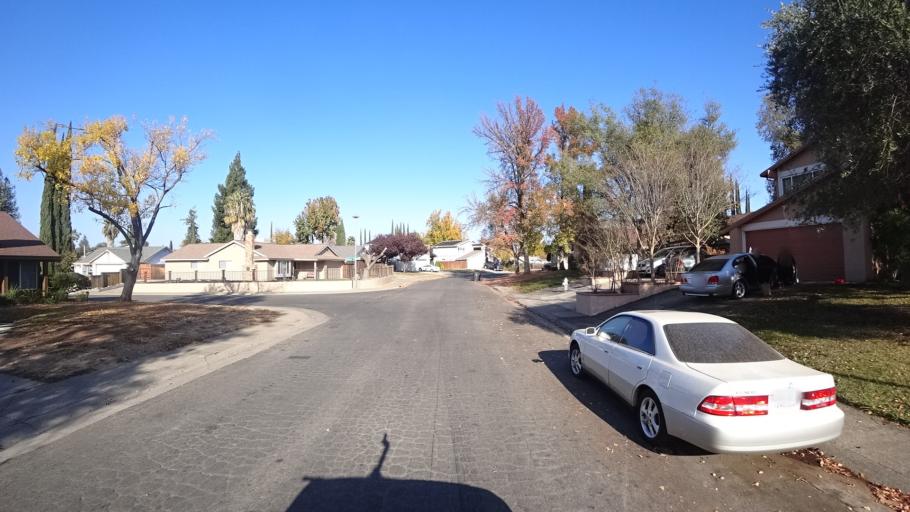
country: US
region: California
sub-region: Sacramento County
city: Fair Oaks
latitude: 38.6754
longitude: -121.2799
